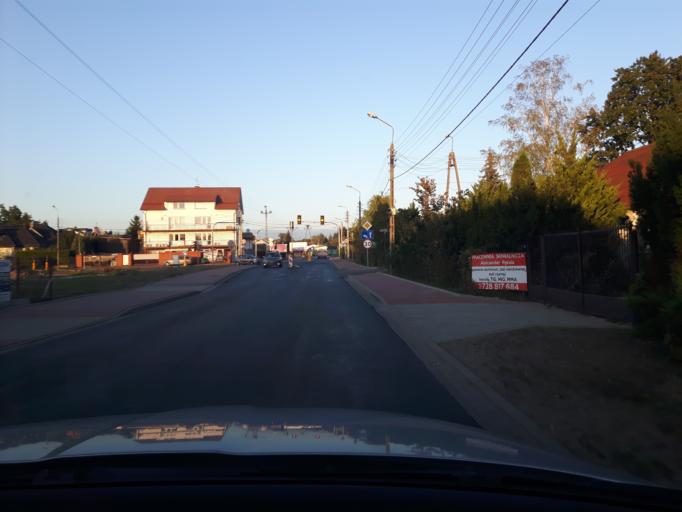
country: PL
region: Masovian Voivodeship
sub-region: Powiat wolominski
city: Kobylka
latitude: 52.3369
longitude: 21.1793
